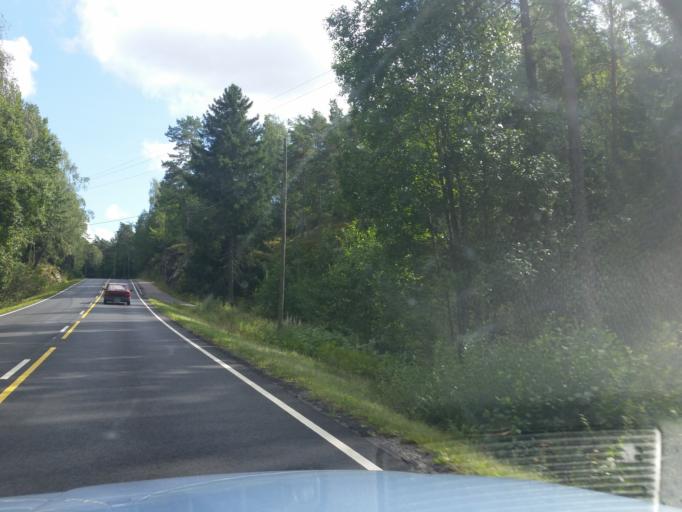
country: FI
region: Varsinais-Suomi
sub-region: Aboland-Turunmaa
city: Laensi-Turunmaa
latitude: 60.2556
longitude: 22.2319
